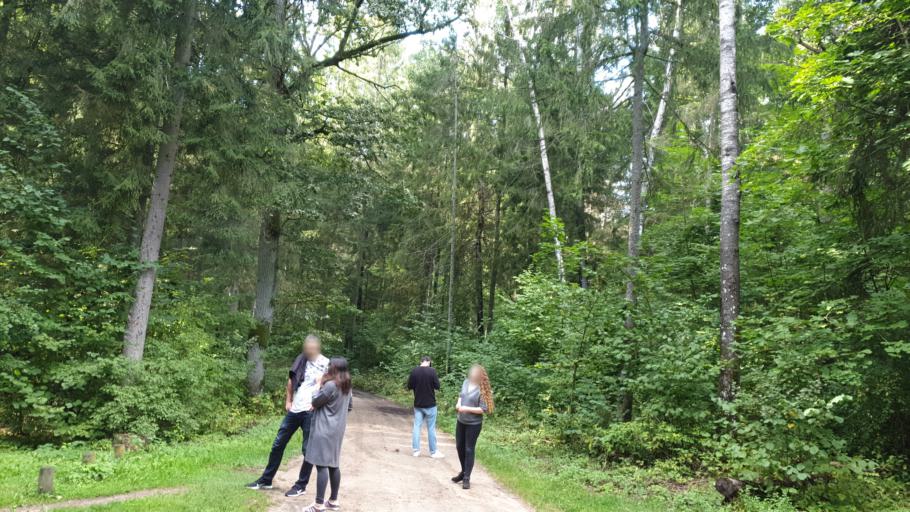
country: LT
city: Trakai
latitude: 54.6464
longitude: 24.9756
